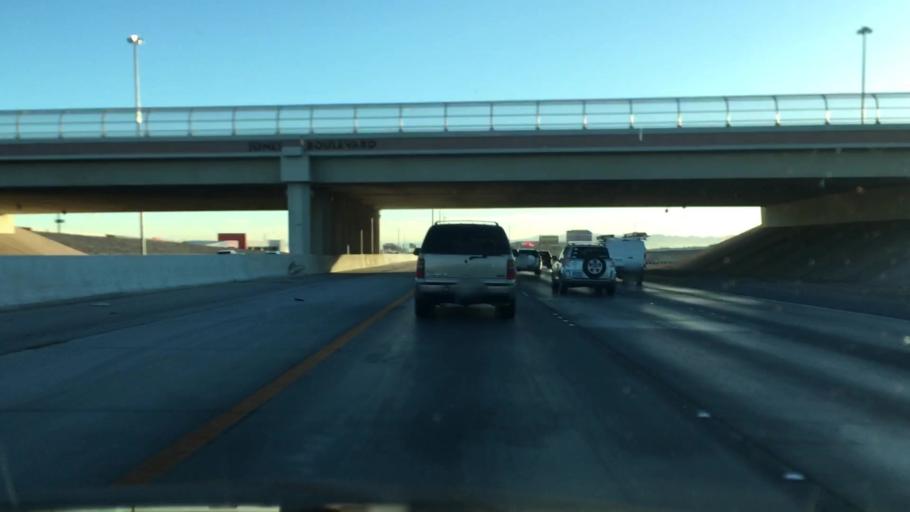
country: US
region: Nevada
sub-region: Clark County
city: Enterprise
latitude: 36.0669
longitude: -115.2251
